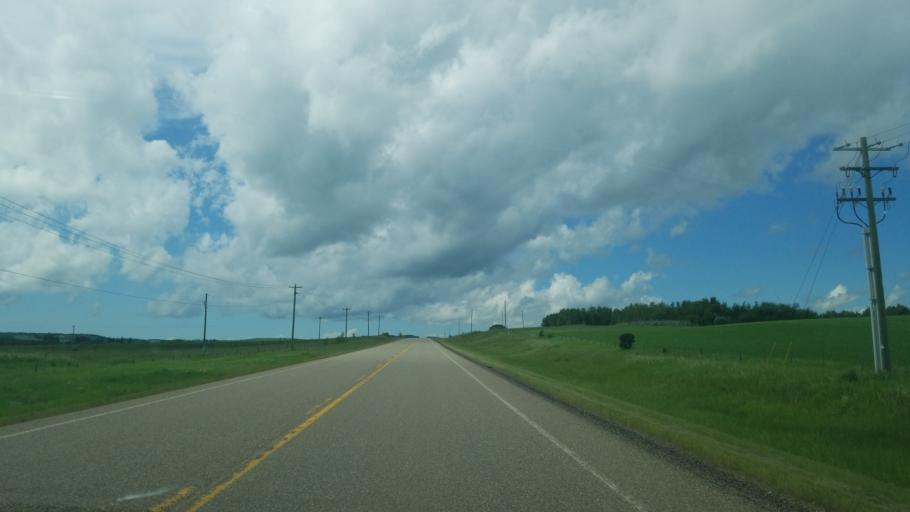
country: CA
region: Saskatchewan
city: Lloydminster
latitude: 53.1617
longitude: -110.1718
